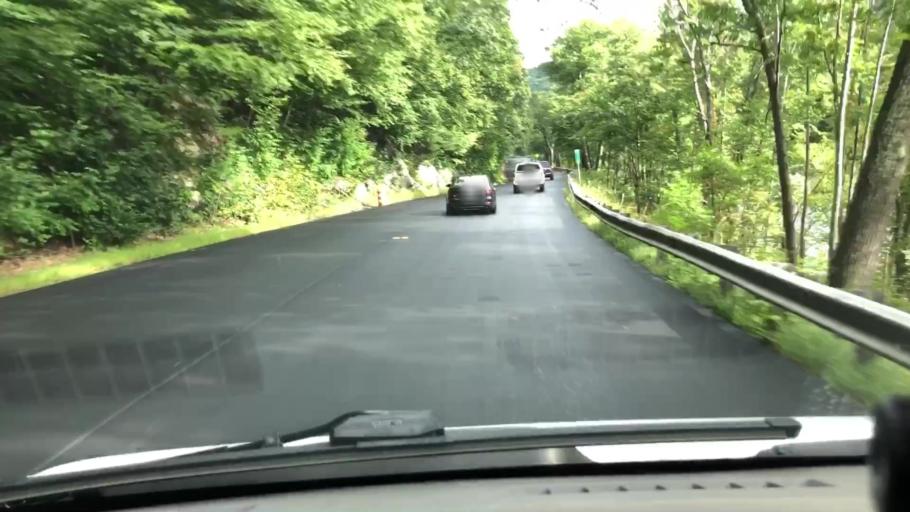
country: US
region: Massachusetts
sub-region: Franklin County
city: Charlemont
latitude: 42.6250
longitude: -72.8512
